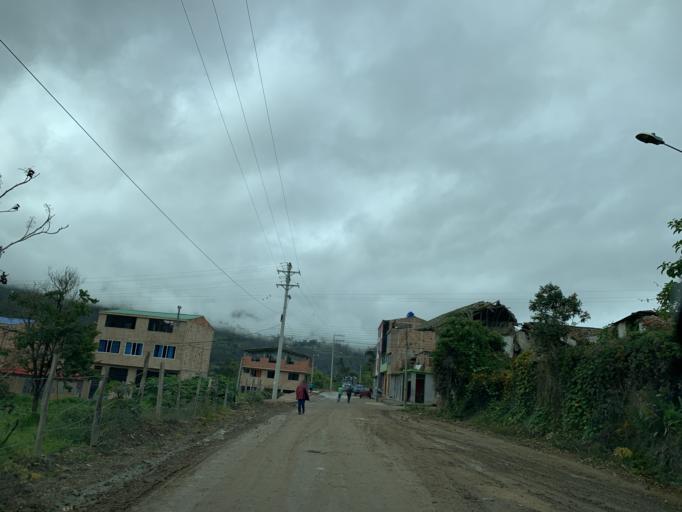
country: CO
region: Boyaca
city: Tibana
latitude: 5.3195
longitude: -73.3948
